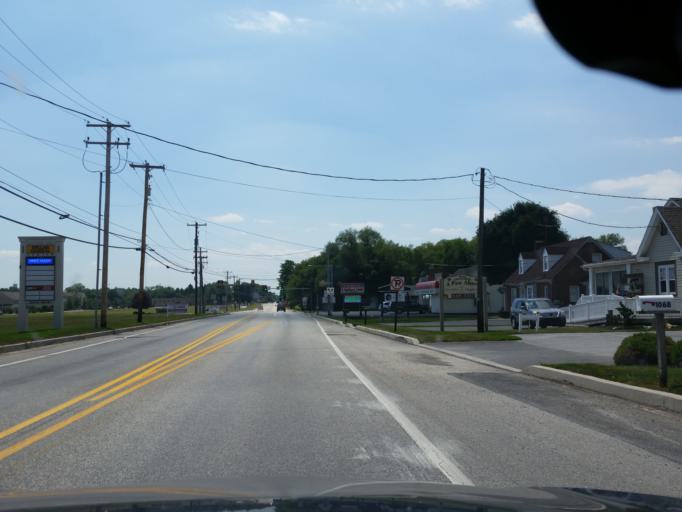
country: US
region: Pennsylvania
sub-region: Cumberland County
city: Schlusser
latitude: 40.2200
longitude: -77.1648
